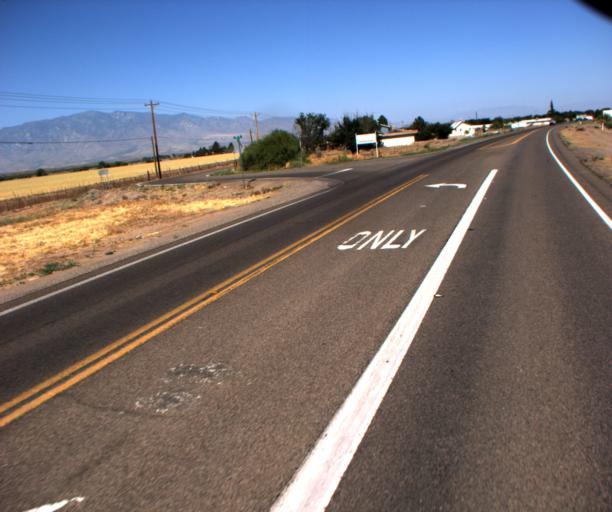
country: US
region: Arizona
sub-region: Graham County
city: Safford
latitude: 32.8131
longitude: -109.6184
